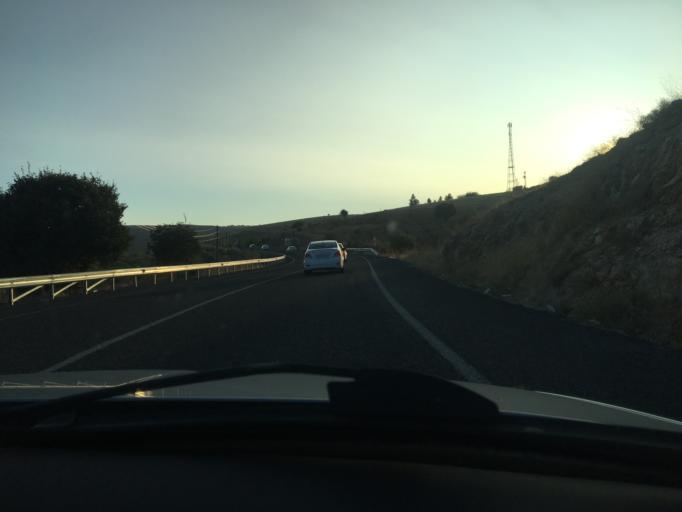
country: TR
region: Sanliurfa
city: Halfeti
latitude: 37.2021
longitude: 37.9693
